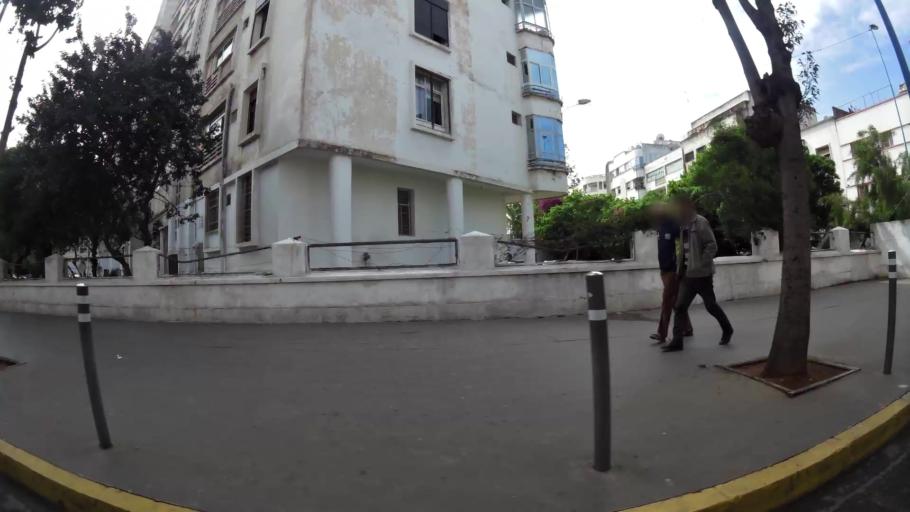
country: MA
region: Grand Casablanca
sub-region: Casablanca
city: Casablanca
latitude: 33.5844
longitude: -7.6308
